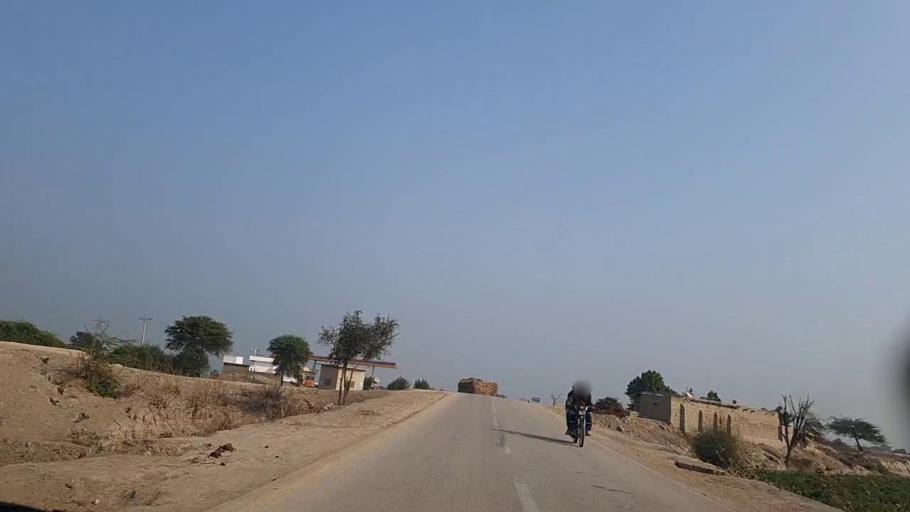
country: PK
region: Sindh
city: Sann
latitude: 26.1451
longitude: 68.1433
